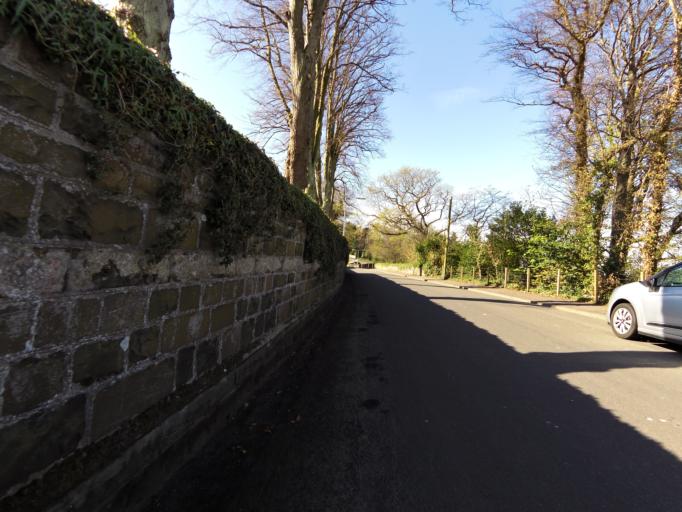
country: GB
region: Scotland
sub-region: Fife
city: Newport-On-Tay
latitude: 56.4372
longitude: -2.9442
